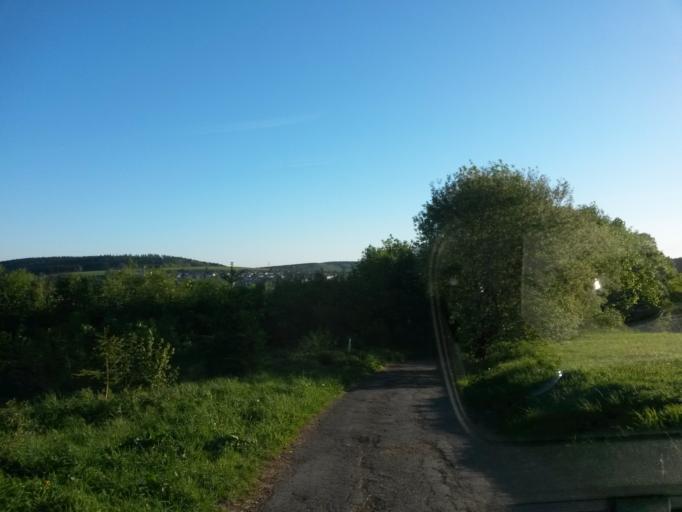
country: DE
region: North Rhine-Westphalia
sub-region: Regierungsbezirk Arnsberg
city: Herscheid
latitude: 51.1709
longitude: 7.7418
